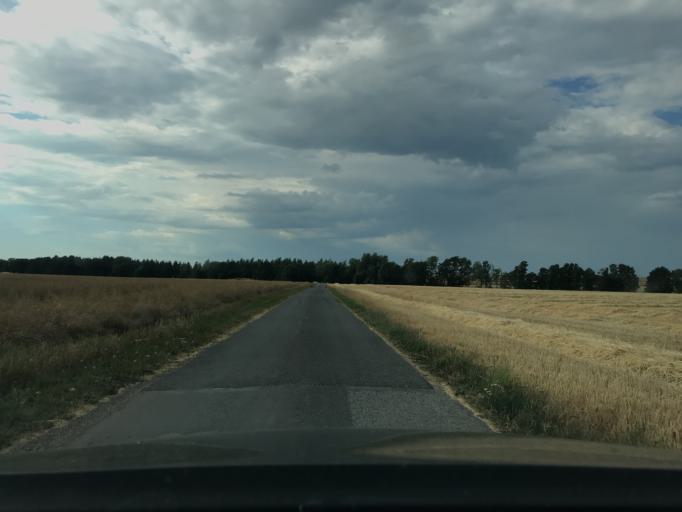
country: SE
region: Skane
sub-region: Simrishamns Kommun
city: Kivik
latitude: 55.5384
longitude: 14.1540
